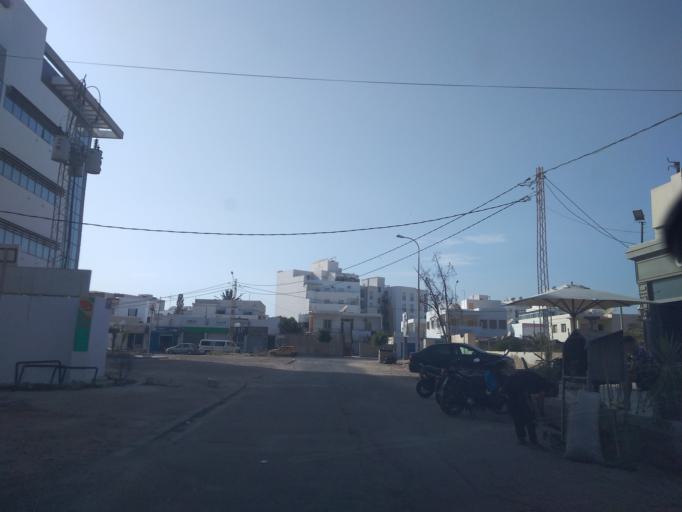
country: TN
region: Safaqis
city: Sfax
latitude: 34.7462
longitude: 10.7675
